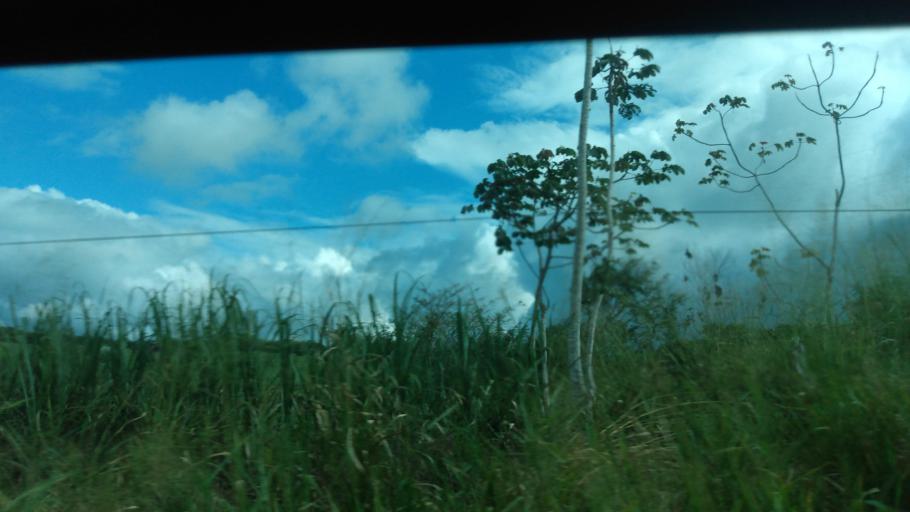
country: BR
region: Pernambuco
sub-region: Quipapa
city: Quipapa
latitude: -8.7790
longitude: -35.9396
